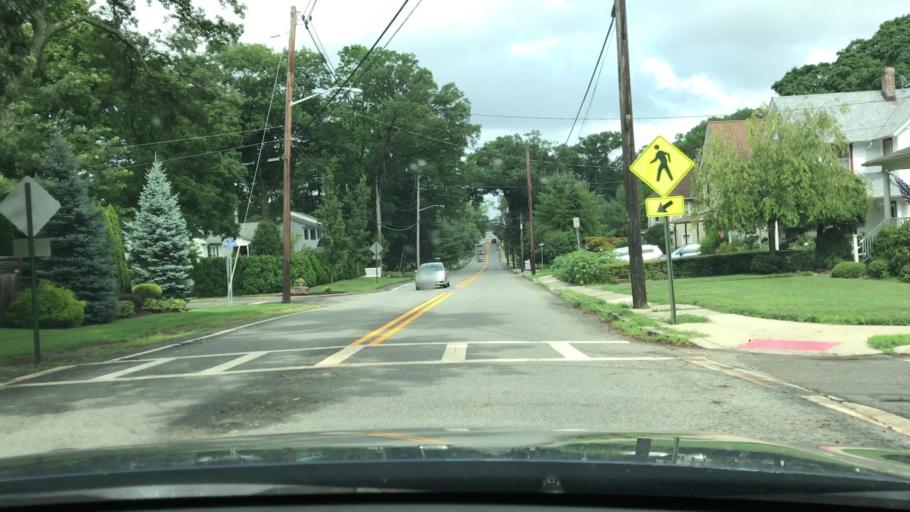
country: US
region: New Jersey
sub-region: Bergen County
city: Ramsey
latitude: 41.0589
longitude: -74.1302
